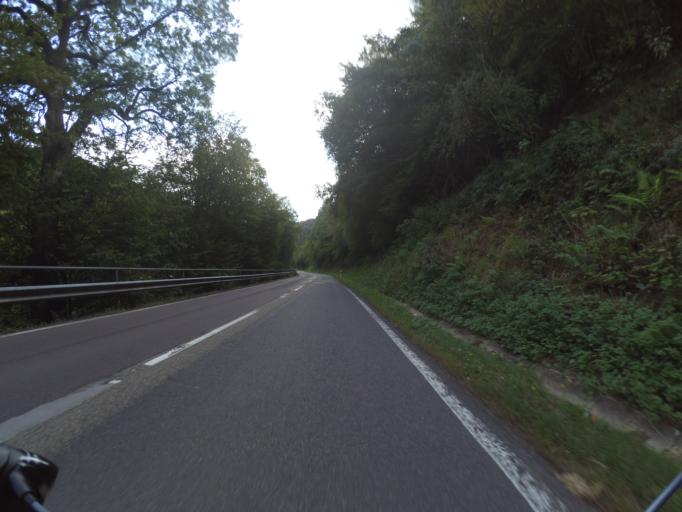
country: DE
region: Rheinland-Pfalz
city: Budlich
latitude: 49.7953
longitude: 6.8982
